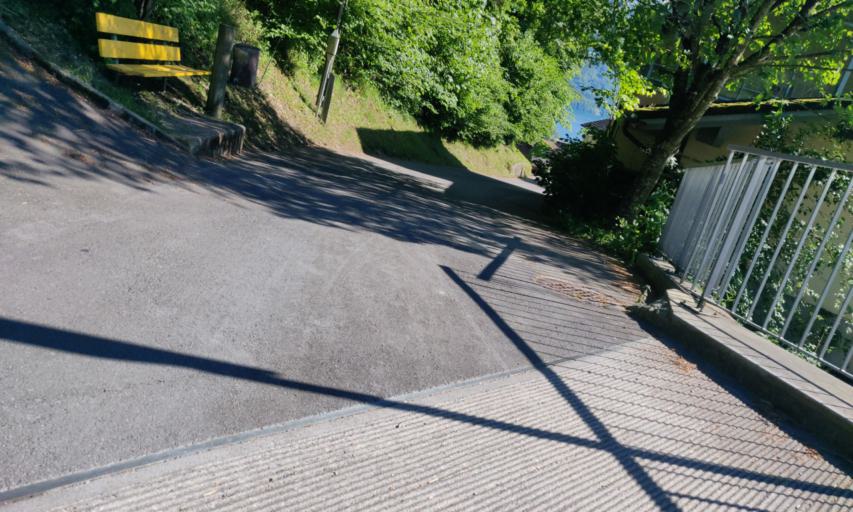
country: CH
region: Schwyz
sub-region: Bezirk Gersau
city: Gersau
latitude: 46.9961
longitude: 8.5278
